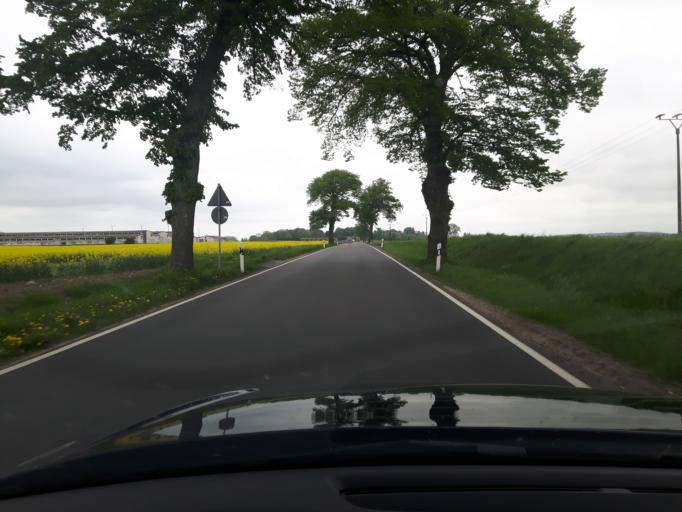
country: DE
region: Mecklenburg-Vorpommern
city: Gnoien
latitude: 54.0206
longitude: 12.6562
